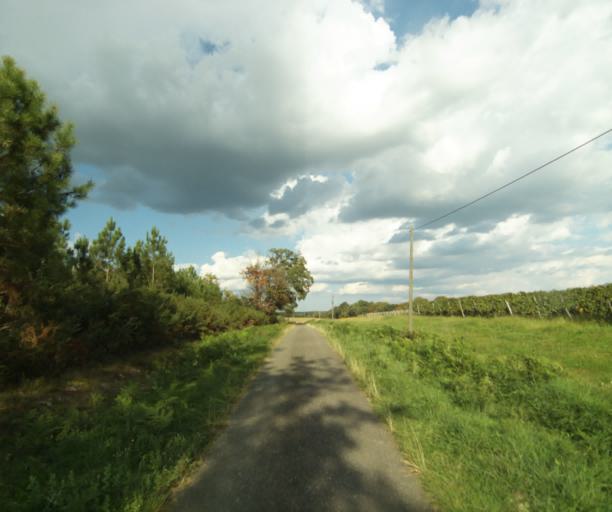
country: FR
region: Midi-Pyrenees
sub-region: Departement du Gers
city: Cazaubon
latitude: 43.8810
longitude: -0.0676
